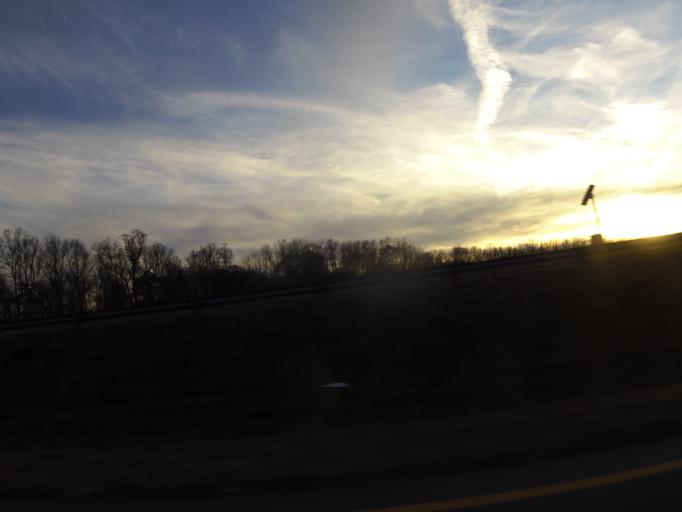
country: US
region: Virginia
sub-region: City of Franklin
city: Franklin
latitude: 36.6845
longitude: -76.9693
